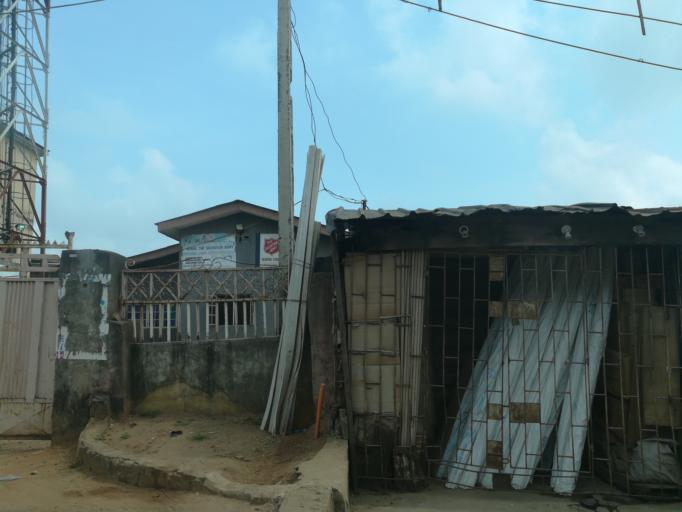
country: NG
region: Lagos
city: Ikorodu
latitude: 6.6185
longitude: 3.5072
